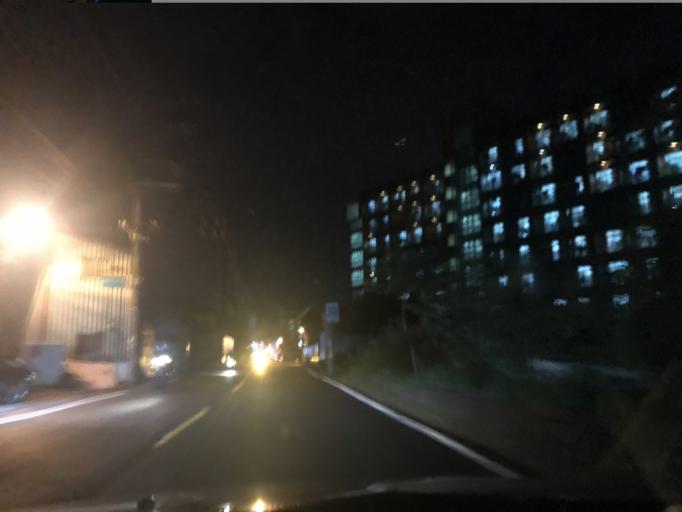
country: TW
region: Taiwan
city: Taoyuan City
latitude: 24.9446
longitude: 121.2334
